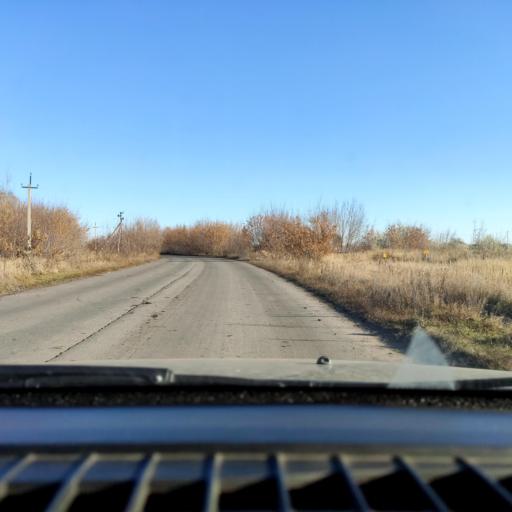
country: RU
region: Samara
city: Tol'yatti
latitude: 53.6394
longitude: 49.3134
